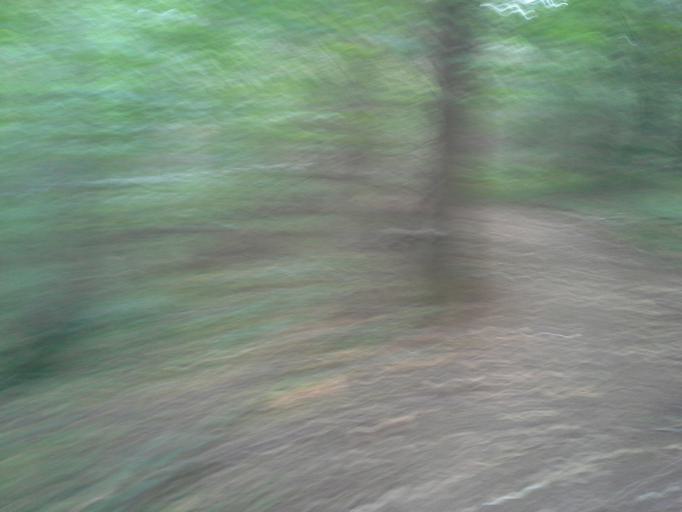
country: RU
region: Moskovskaya
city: Selyatino
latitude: 55.5519
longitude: 37.0012
